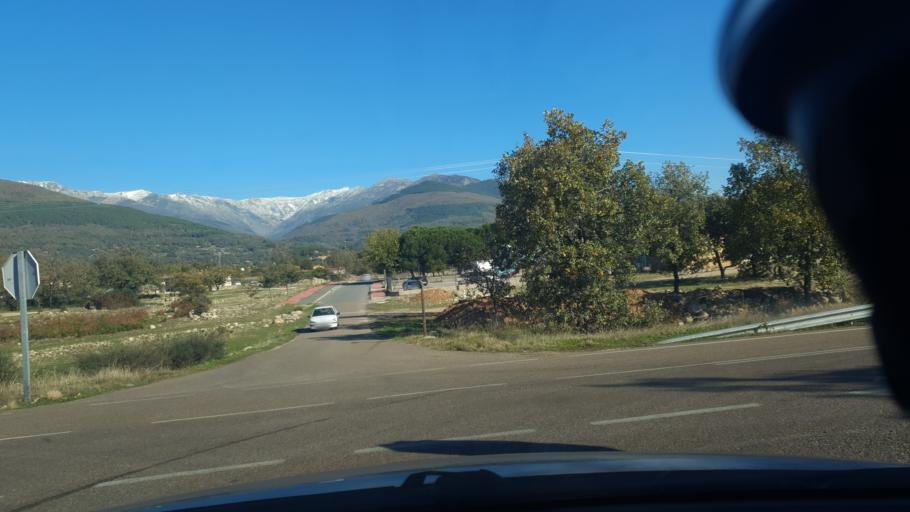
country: ES
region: Castille and Leon
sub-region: Provincia de Avila
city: Candeleda
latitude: 40.1404
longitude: -5.2585
